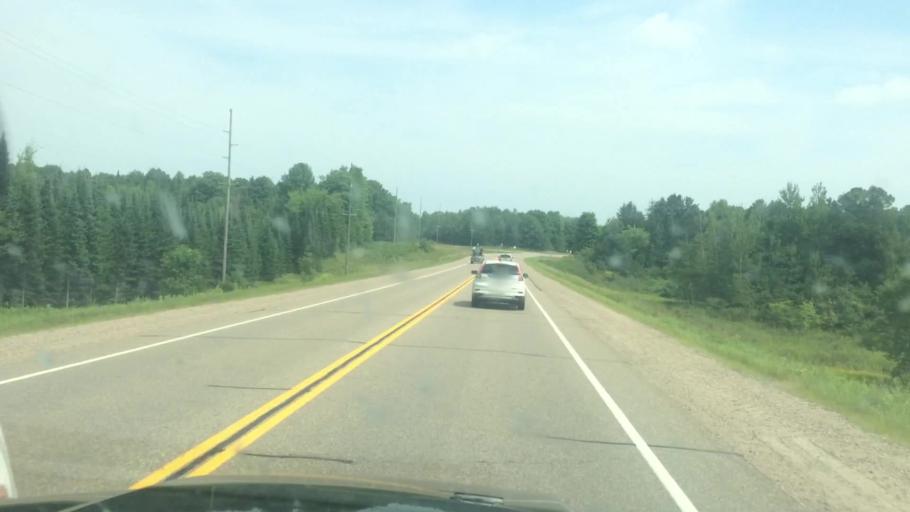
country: US
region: Wisconsin
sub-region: Langlade County
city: Antigo
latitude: 45.1643
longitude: -89.0132
